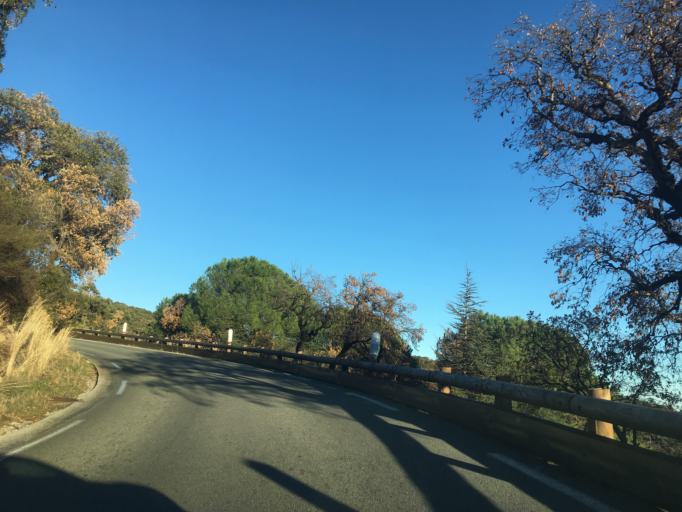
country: FR
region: Provence-Alpes-Cote d'Azur
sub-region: Departement du Var
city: Le Plan-de-la-Tour
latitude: 43.2958
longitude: 6.5602
